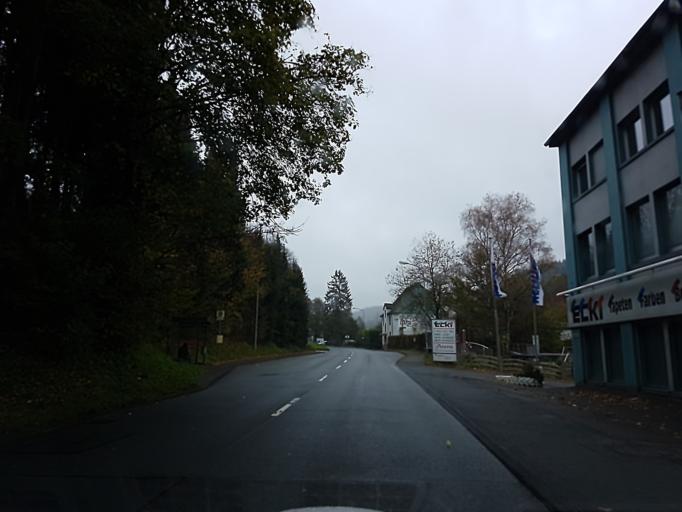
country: DE
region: North Rhine-Westphalia
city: Kierspe
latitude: 51.1278
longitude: 7.6217
